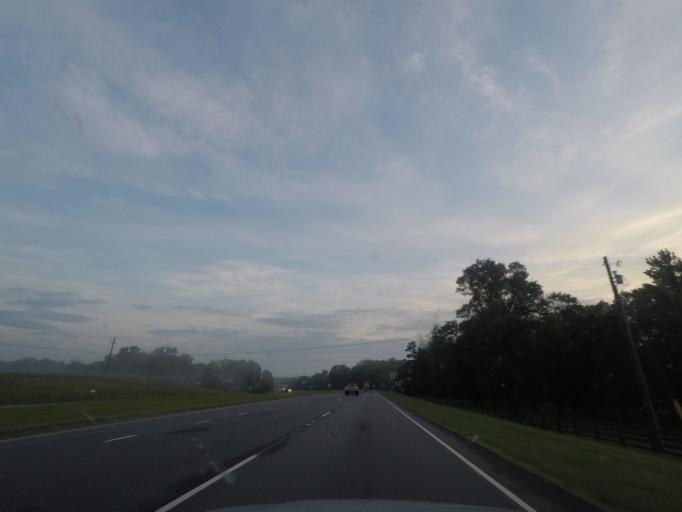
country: US
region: North Carolina
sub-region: Person County
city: Roxboro
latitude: 36.2378
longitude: -78.9324
